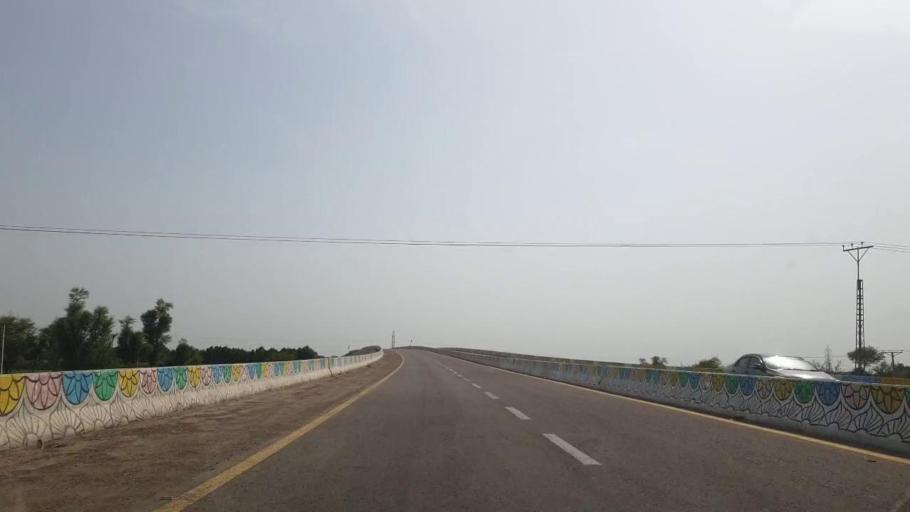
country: PK
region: Sindh
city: Sakrand
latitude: 26.1574
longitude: 68.2527
